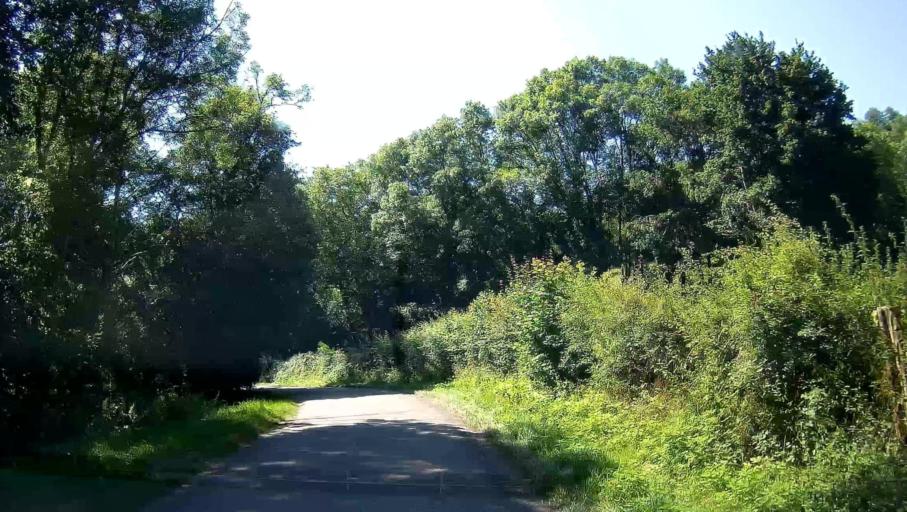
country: FR
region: Bourgogne
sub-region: Departement de la Cote-d'Or
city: Nolay
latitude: 46.9811
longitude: 4.6436
